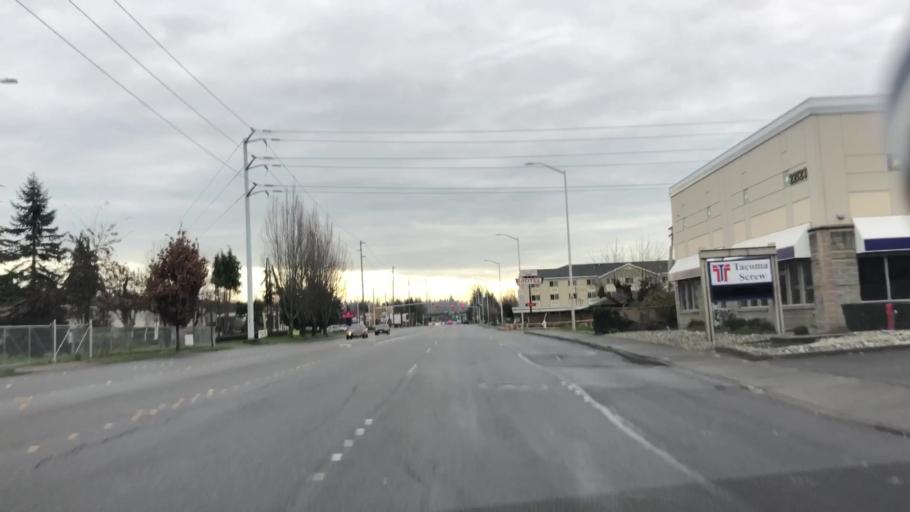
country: US
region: Washington
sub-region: King County
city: Kent
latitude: 47.4033
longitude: -122.2281
